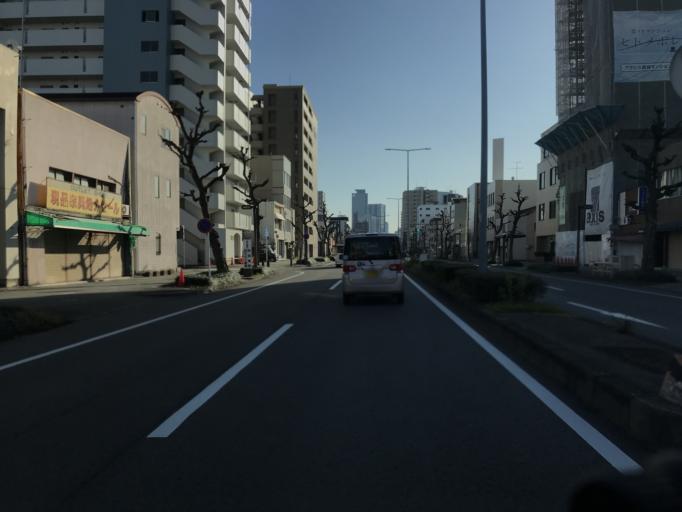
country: JP
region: Aichi
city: Nagoya-shi
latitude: 35.1906
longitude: 136.8870
